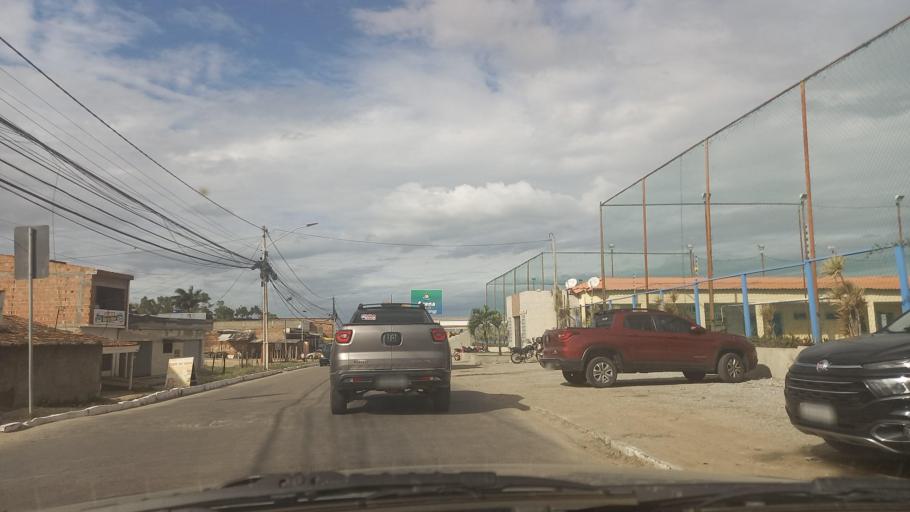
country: BR
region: Pernambuco
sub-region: Caruaru
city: Caruaru
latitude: -8.2870
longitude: -36.0037
